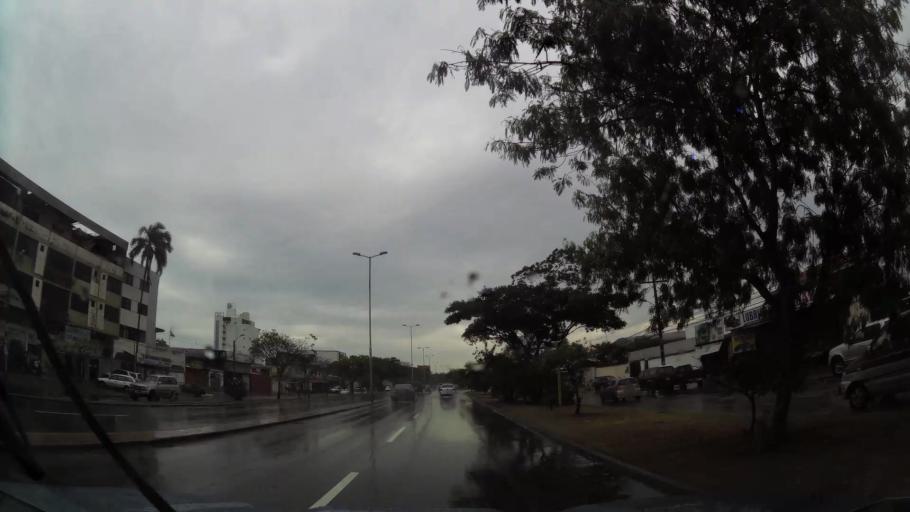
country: BO
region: Santa Cruz
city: Santa Cruz de la Sierra
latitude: -17.7932
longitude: -63.1656
